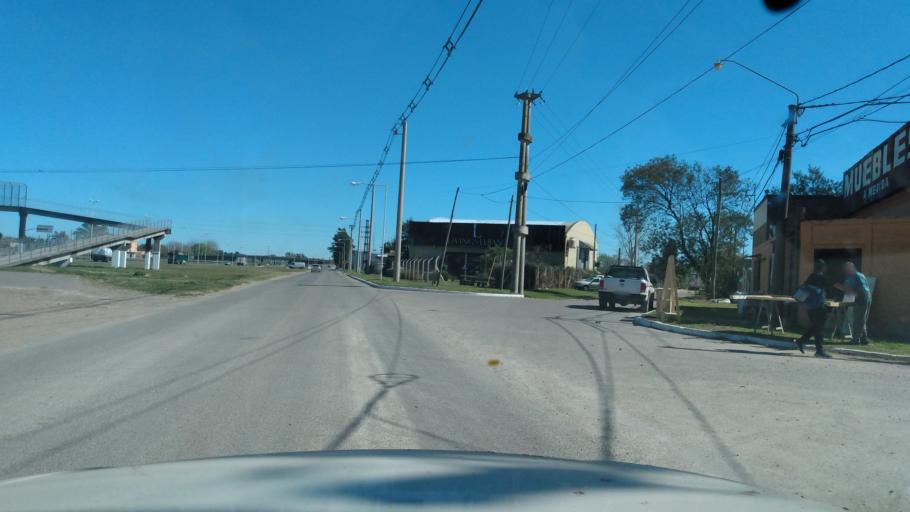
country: AR
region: Buenos Aires
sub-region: Partido de Lujan
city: Lujan
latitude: -34.5541
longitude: -59.1030
